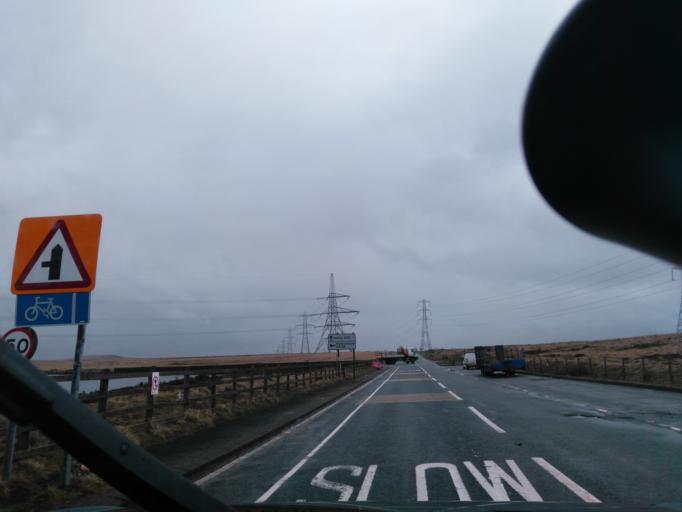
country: GB
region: England
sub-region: Borough of Rochdale
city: Littleborough
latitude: 53.6591
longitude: -2.0411
